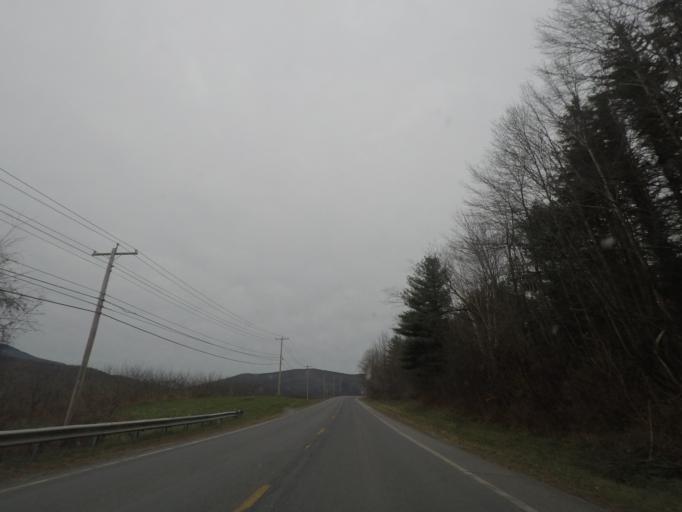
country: US
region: Massachusetts
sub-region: Berkshire County
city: Williamstown
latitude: 42.6689
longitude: -73.2383
